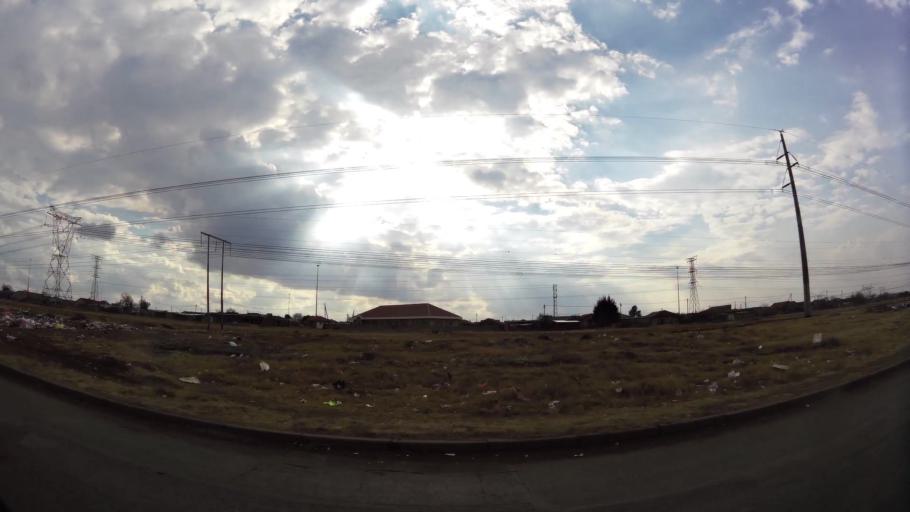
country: ZA
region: Gauteng
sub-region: Sedibeng District Municipality
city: Vereeniging
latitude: -26.6761
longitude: 27.8764
